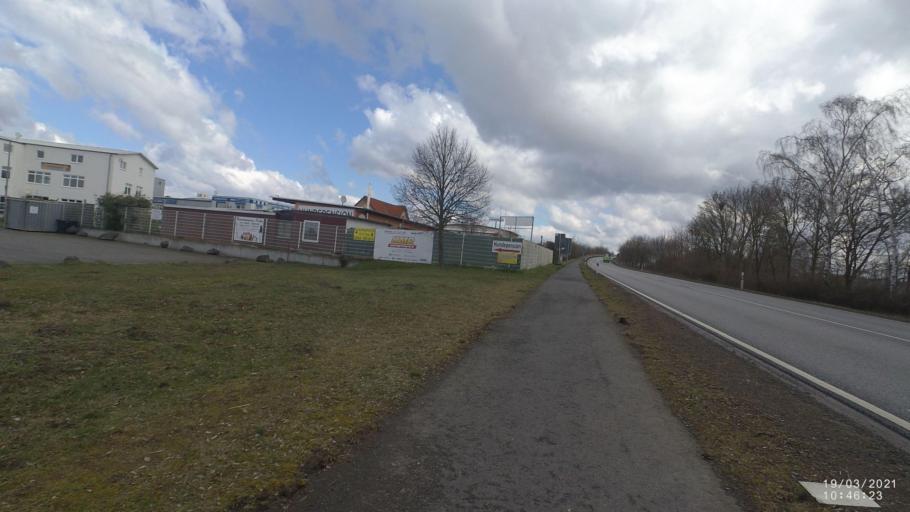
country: DE
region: Rheinland-Pfalz
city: Mendig
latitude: 50.3654
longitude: 7.2979
